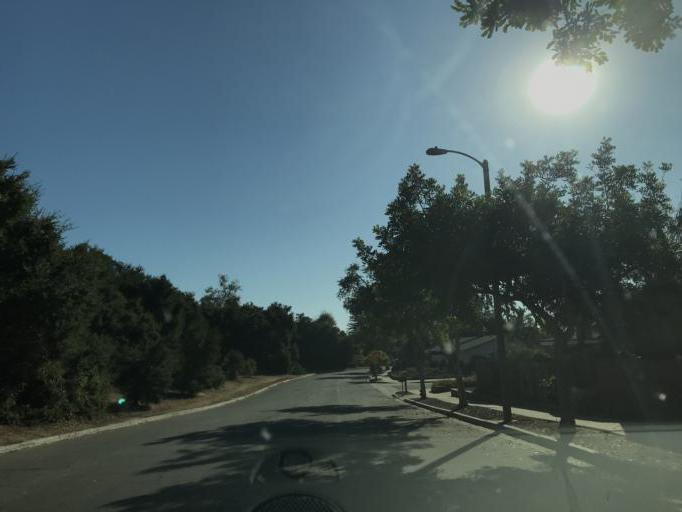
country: US
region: California
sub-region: Santa Barbara County
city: Goleta
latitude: 34.4576
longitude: -119.8108
